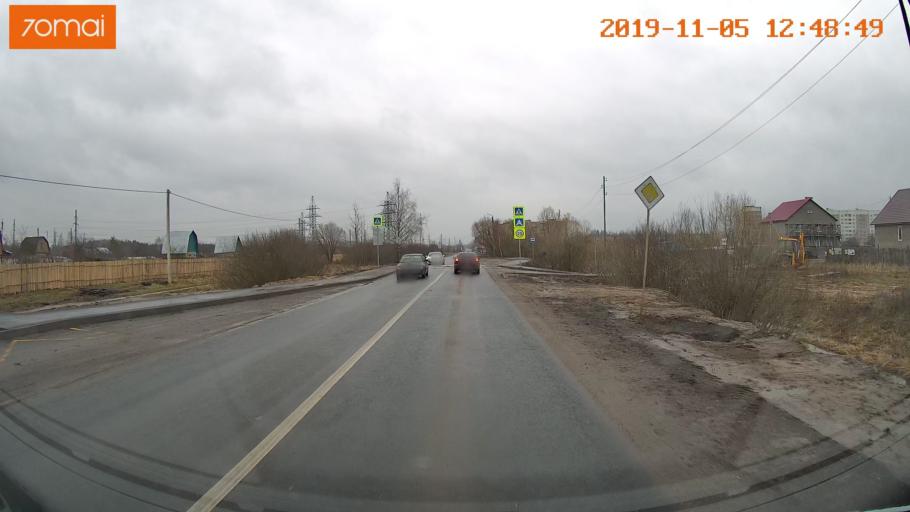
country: RU
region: Ivanovo
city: Kokhma
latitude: 56.9581
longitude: 41.1011
